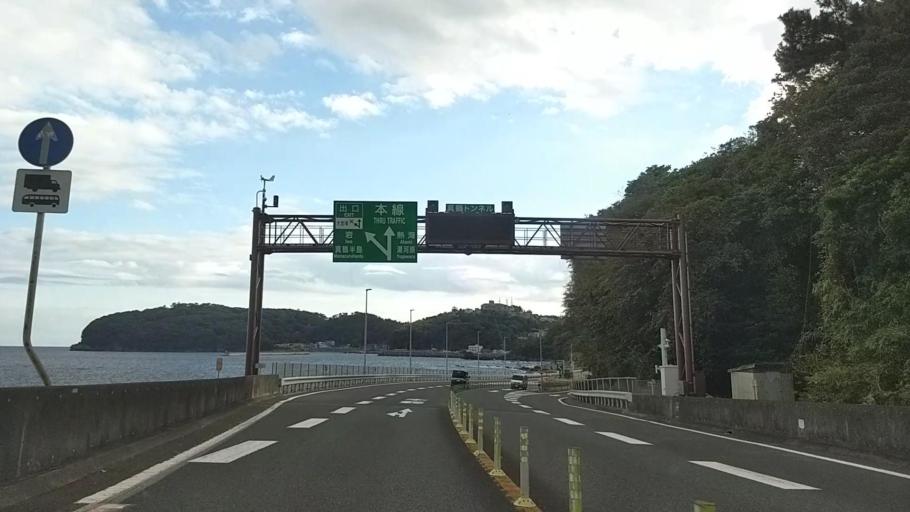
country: JP
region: Kanagawa
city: Yugawara
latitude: 35.1594
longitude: 139.1439
